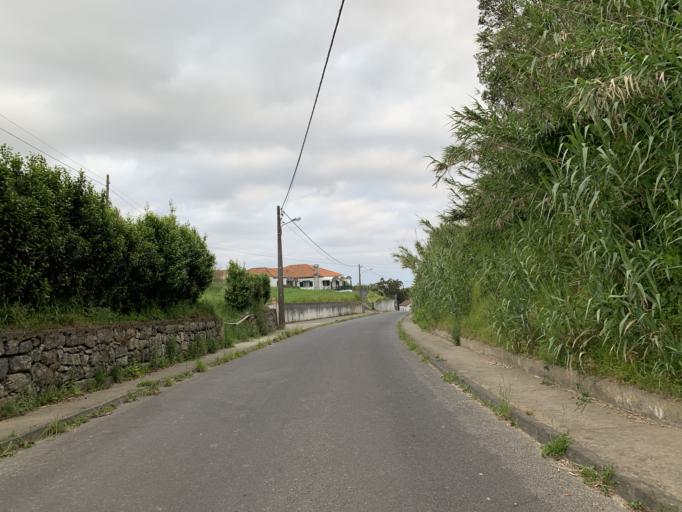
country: PT
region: Azores
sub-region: Ponta Delgada
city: Arrifes
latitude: 37.8463
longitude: -25.8399
